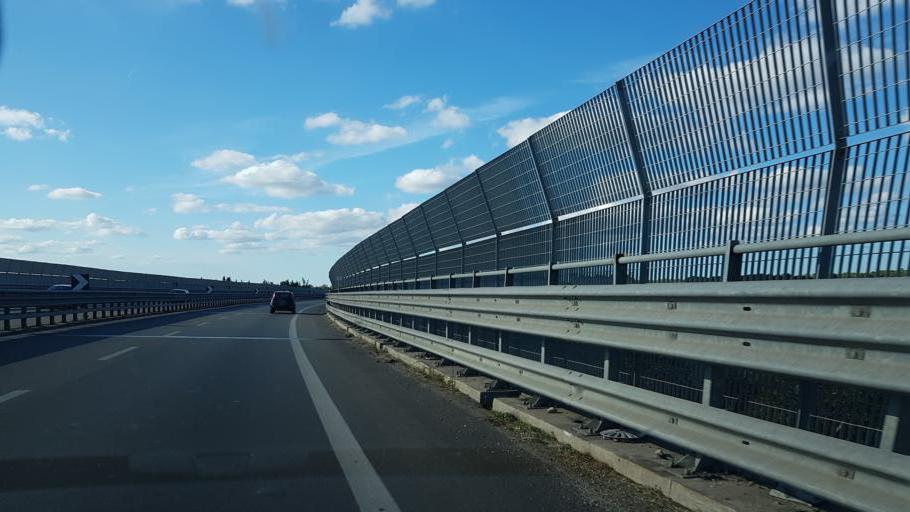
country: IT
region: Apulia
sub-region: Provincia di Lecce
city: Lequile
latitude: 40.3278
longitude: 18.1434
